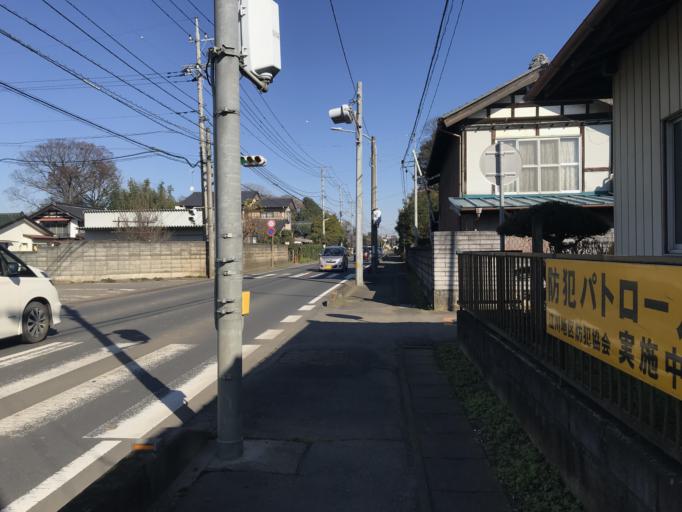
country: JP
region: Ibaraki
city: Yuki
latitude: 36.2664
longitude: 139.8422
